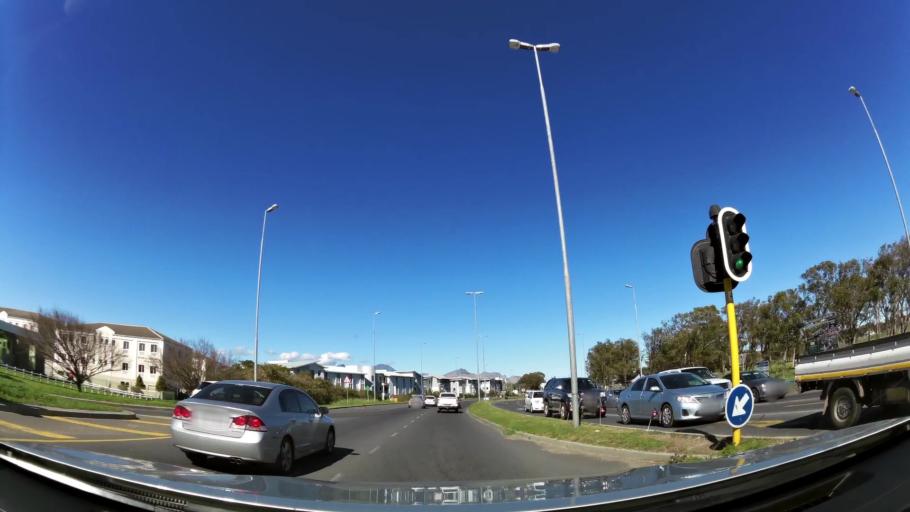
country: ZA
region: Western Cape
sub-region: Cape Winelands District Municipality
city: Stellenbosch
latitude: -34.0850
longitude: 18.8200
